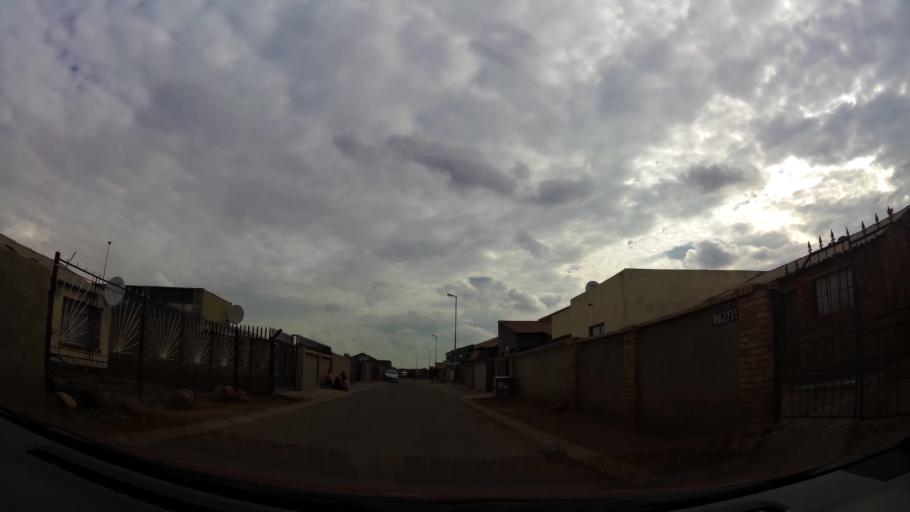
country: ZA
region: Gauteng
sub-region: City of Johannesburg Metropolitan Municipality
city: Soweto
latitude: -26.2426
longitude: 27.8376
